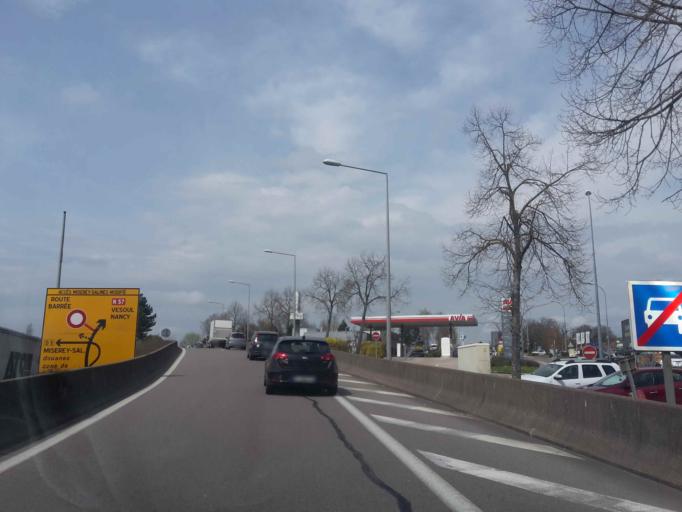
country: FR
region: Franche-Comte
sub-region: Departement du Doubs
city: Miserey-Salines
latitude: 47.2762
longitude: 5.9945
